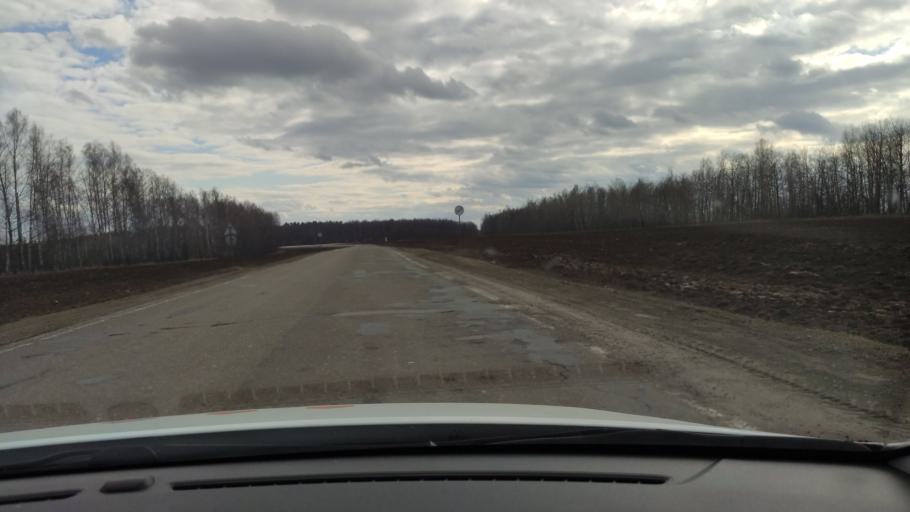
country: RU
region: Tatarstan
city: Vysokaya Gora
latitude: 56.0910
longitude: 49.1804
